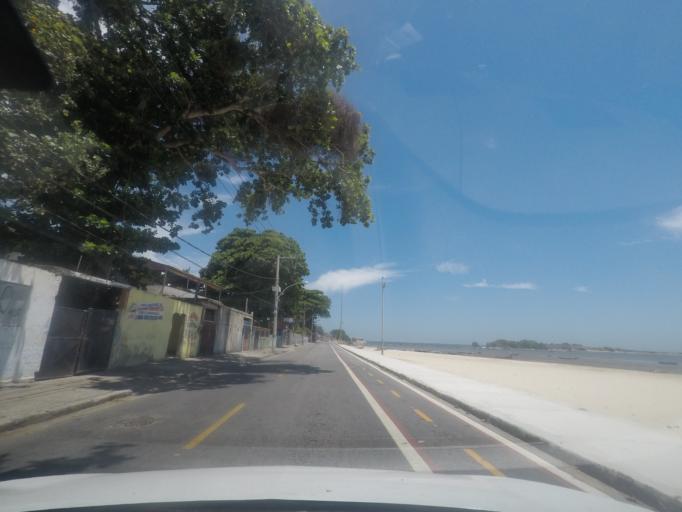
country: BR
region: Rio de Janeiro
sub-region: Itaguai
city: Itaguai
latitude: -22.9790
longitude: -43.7037
